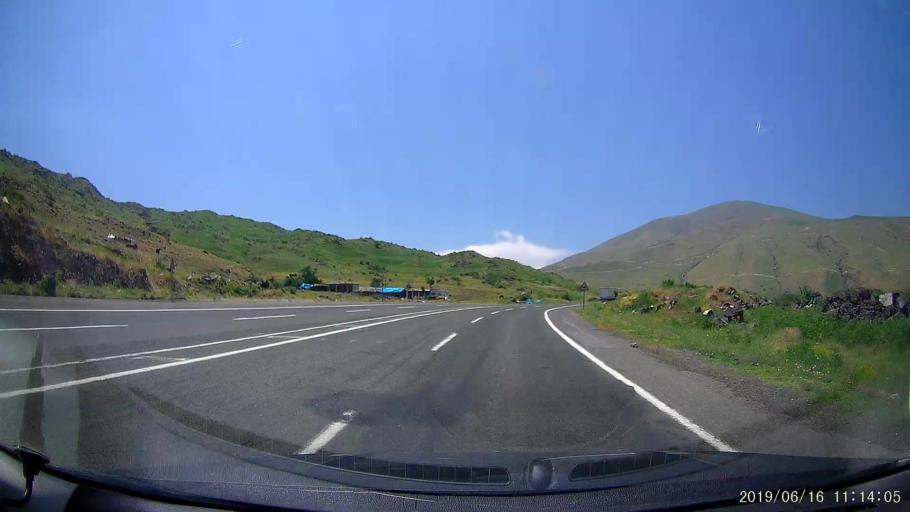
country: TR
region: Igdir
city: Igdir
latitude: 39.7836
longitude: 44.1457
